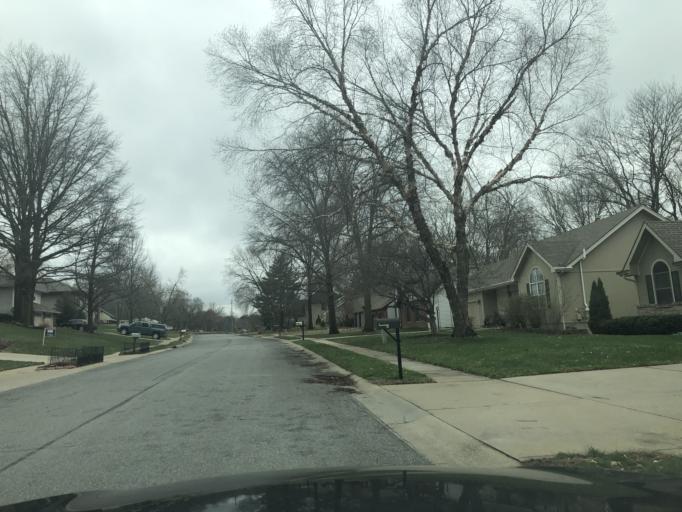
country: US
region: Kansas
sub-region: Leavenworth County
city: Leavenworth
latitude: 39.2845
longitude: -94.9150
